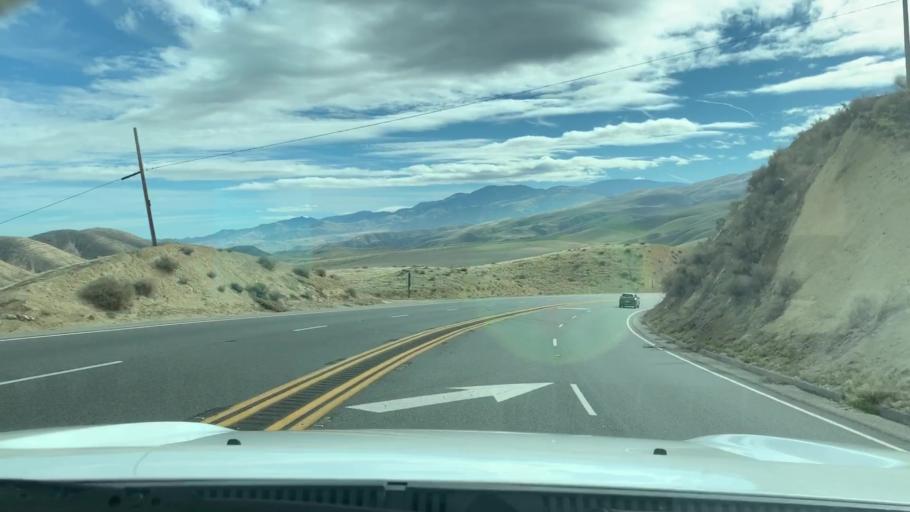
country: US
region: California
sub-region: Kern County
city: Maricopa
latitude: 35.0046
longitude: -119.4165
